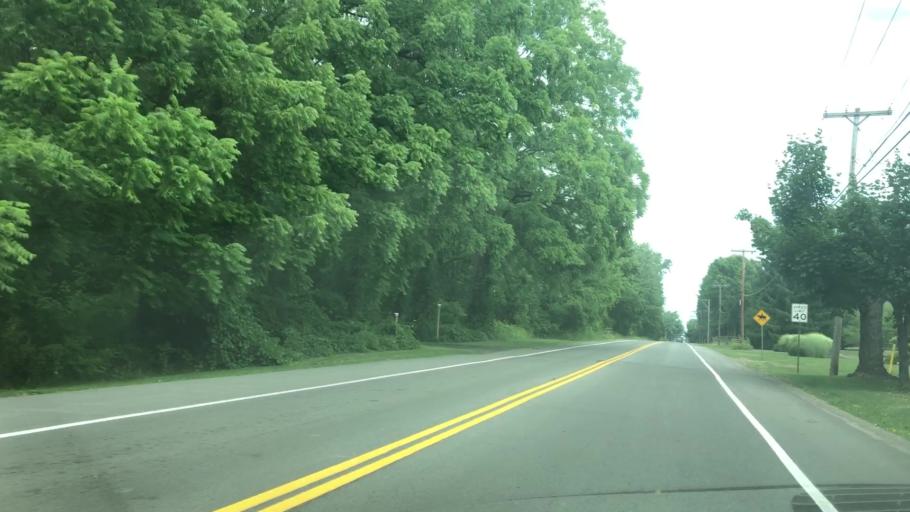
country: US
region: New York
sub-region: Monroe County
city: Fairport
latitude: 43.1308
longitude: -77.4006
